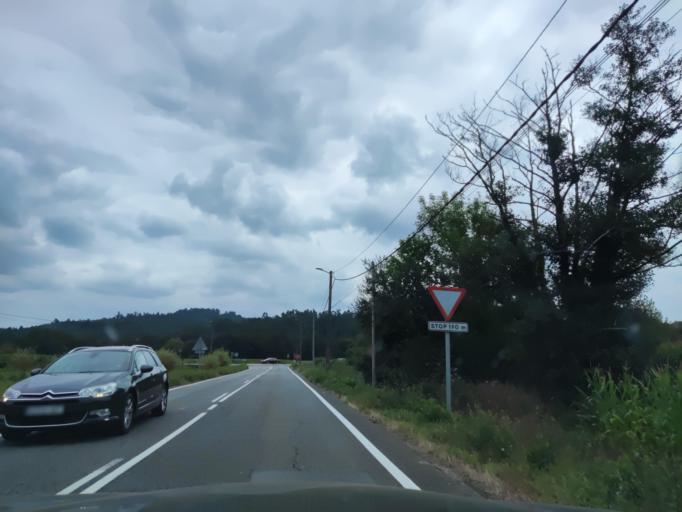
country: ES
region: Galicia
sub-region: Provincia da Coruna
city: Teo
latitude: 42.7651
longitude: -8.5494
